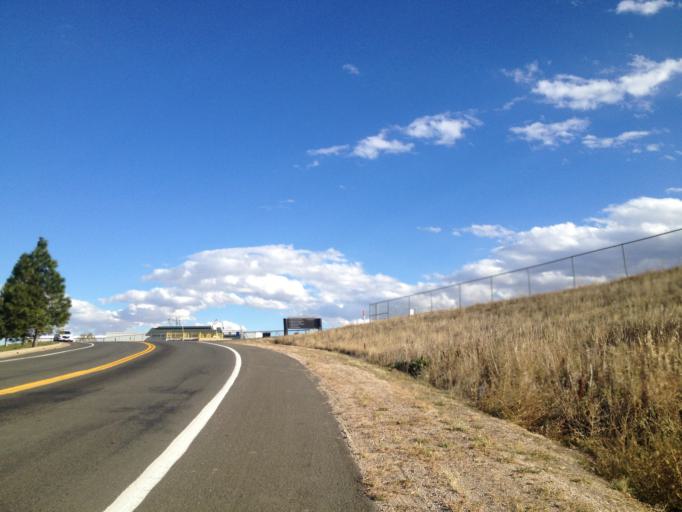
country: US
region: Colorado
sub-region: Broomfield County
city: Broomfield
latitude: 39.9143
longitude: -105.1219
